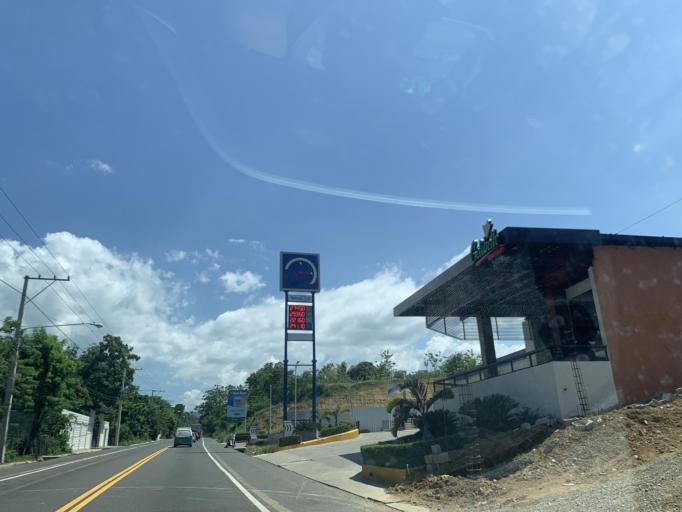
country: DO
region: Puerto Plata
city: Imbert
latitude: 19.7171
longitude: -70.8341
